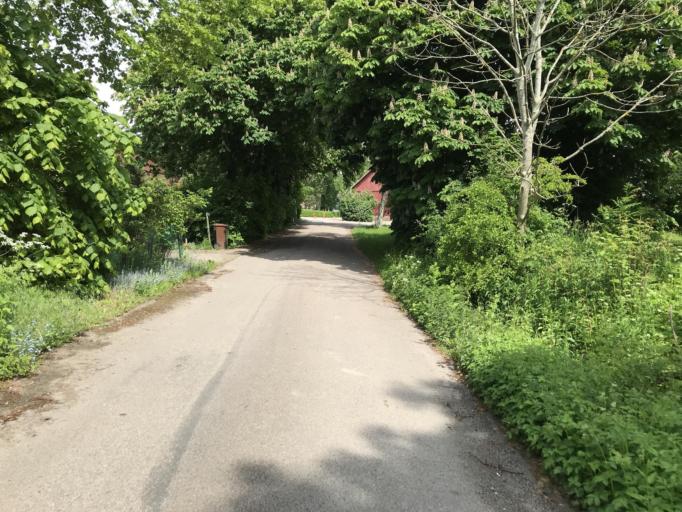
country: SE
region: Skane
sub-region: Landskrona
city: Landskrona
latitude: 55.9041
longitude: 12.8490
